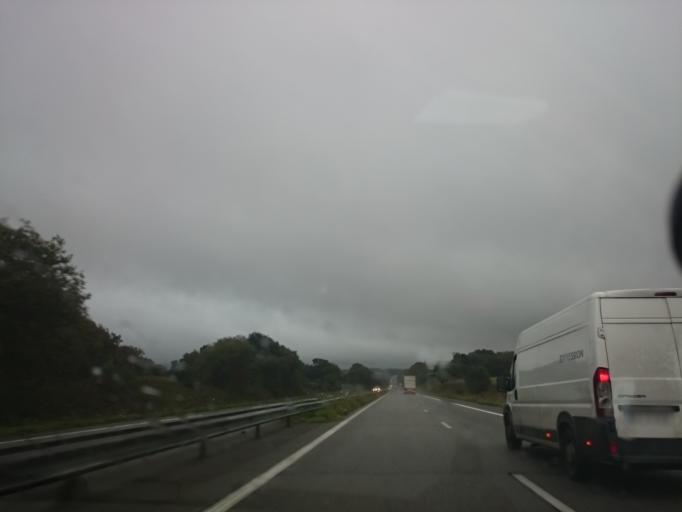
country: FR
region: Brittany
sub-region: Departement du Finistere
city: Briec
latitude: 48.1480
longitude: -4.0342
